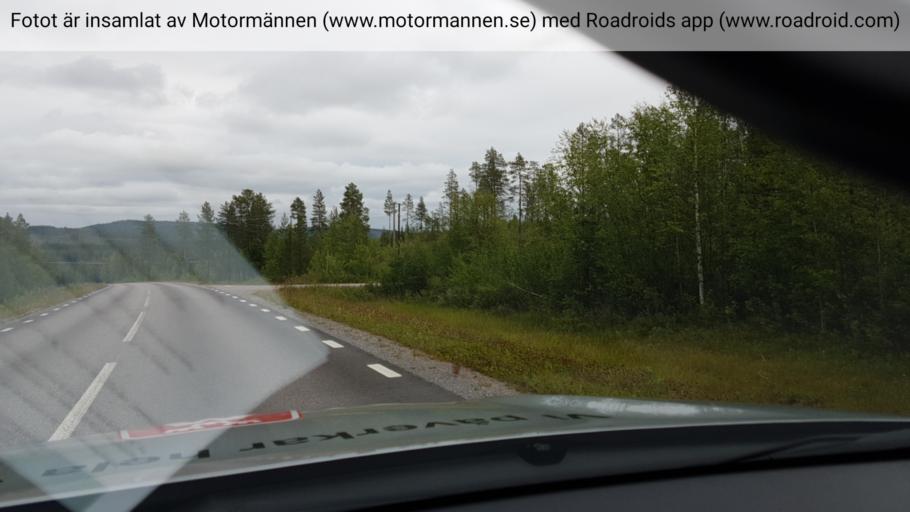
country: SE
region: Norrbotten
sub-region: Gallivare Kommun
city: Gaellivare
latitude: 67.0706
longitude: 21.3215
